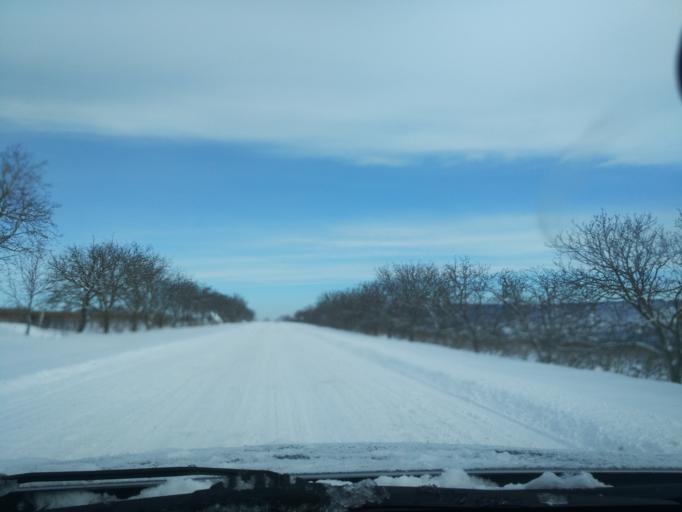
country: MD
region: Nisporeni
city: Nisporeni
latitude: 47.1178
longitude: 28.1553
